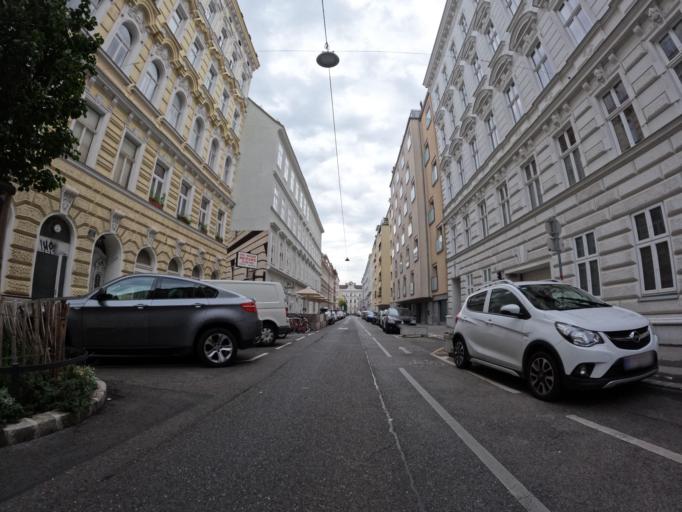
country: AT
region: Vienna
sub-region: Wien Stadt
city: Vienna
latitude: 48.2029
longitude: 16.3439
